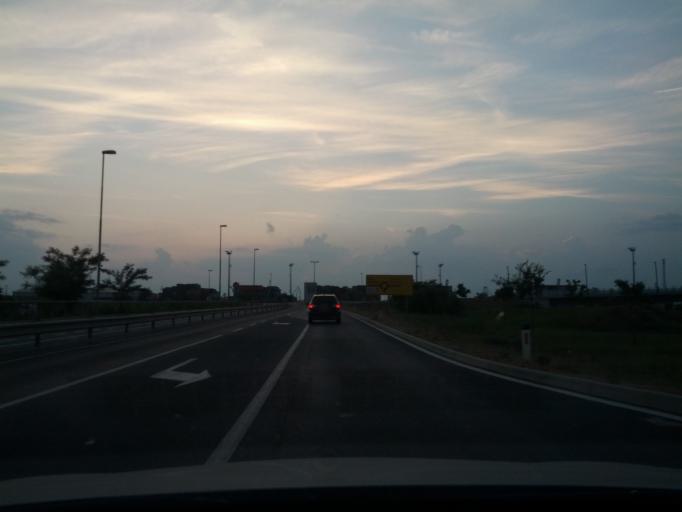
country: SI
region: Koper-Capodistria
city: Prade
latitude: 45.5535
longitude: 13.7560
